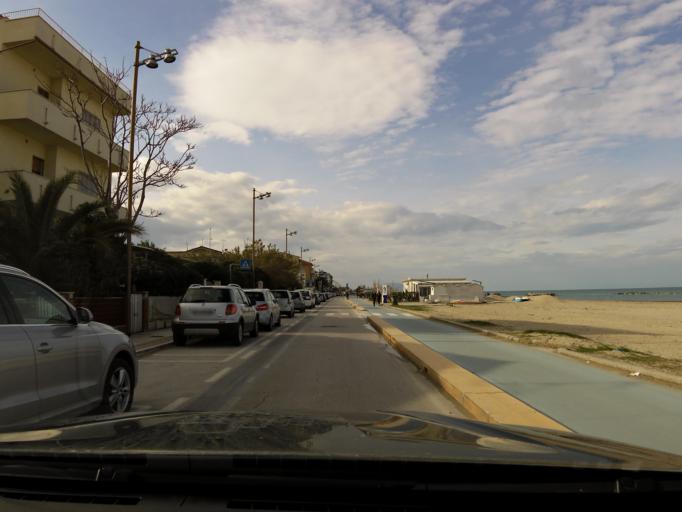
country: IT
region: The Marches
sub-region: Provincia di Macerata
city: Civitanova Marche
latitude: 43.3251
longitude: 13.7170
